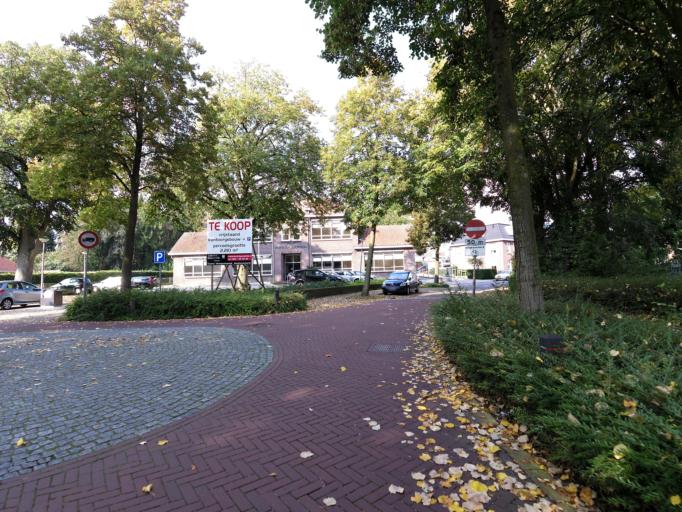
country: NL
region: Gelderland
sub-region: Gemeente Aalten
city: Aalten
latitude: 51.9253
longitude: 6.5795
